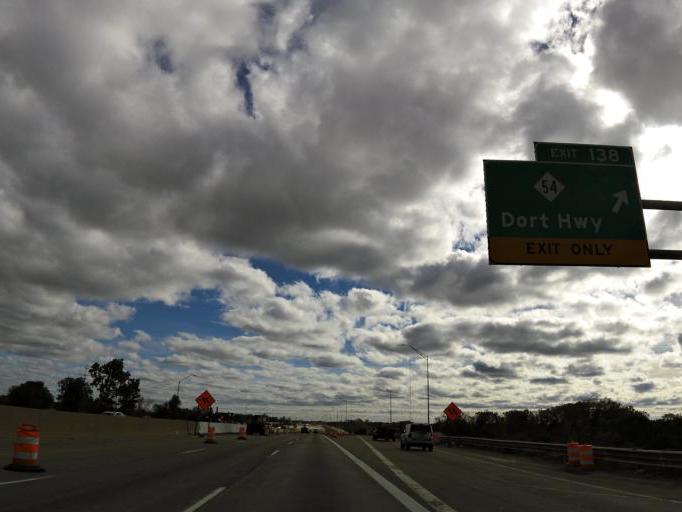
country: US
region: Michigan
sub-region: Genesee County
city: Flint
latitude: 43.0116
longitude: -83.6606
